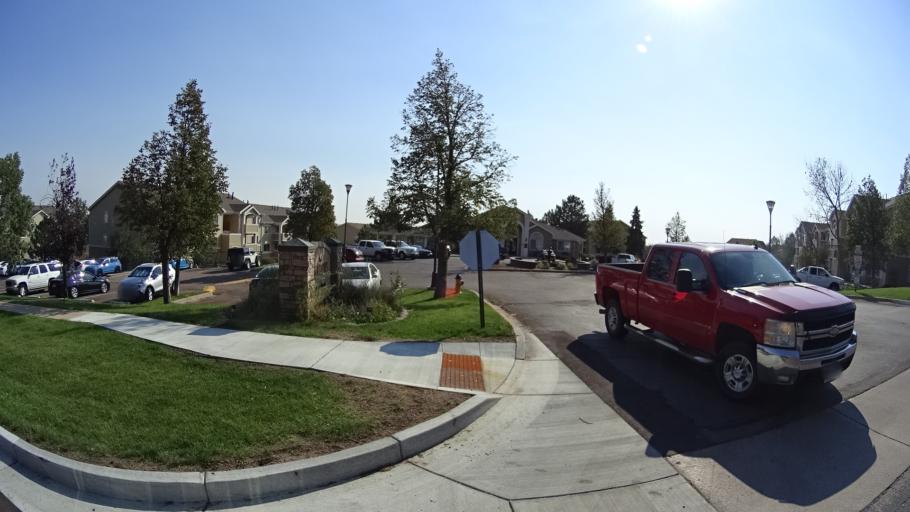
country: US
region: Colorado
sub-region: El Paso County
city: Stratmoor
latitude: 38.7713
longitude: -104.8105
